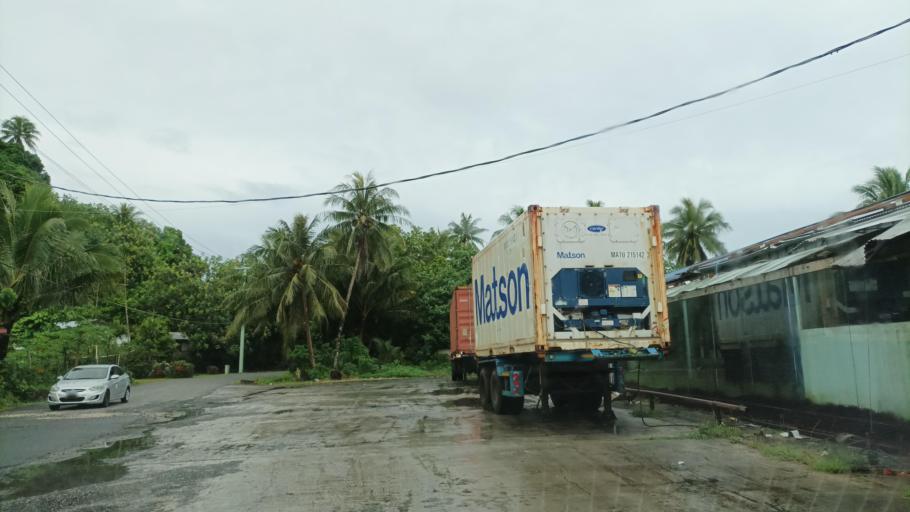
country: FM
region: Kosrae
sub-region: Tafunsak Municipality
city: Tafunsak
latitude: 5.3686
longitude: 162.9953
